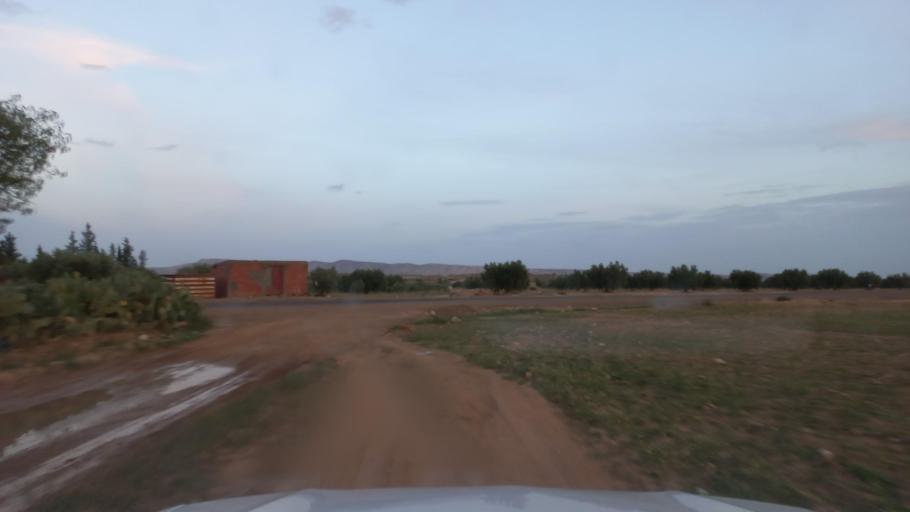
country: TN
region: Al Qasrayn
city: Sbiba
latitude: 35.3475
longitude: 9.0531
